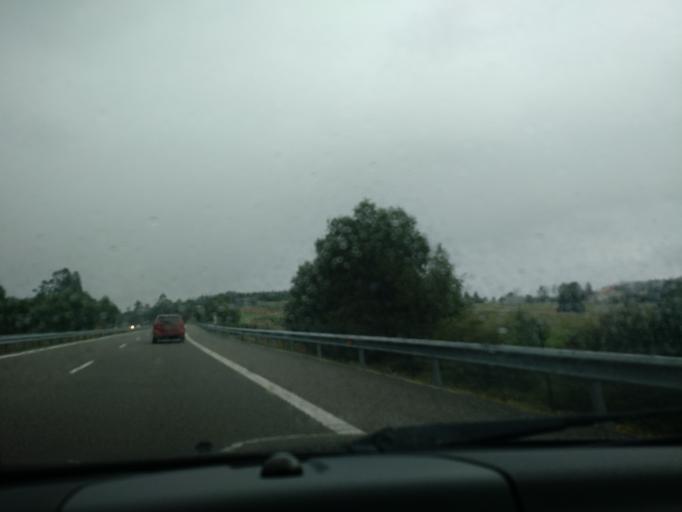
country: ES
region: Galicia
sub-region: Provincia da Coruna
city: Mesia
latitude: 43.1354
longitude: -8.3307
